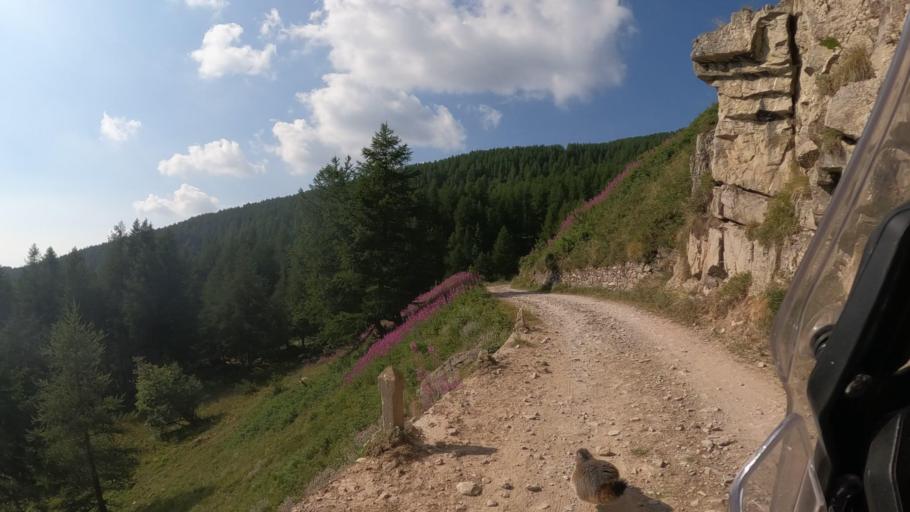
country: IT
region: Piedmont
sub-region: Provincia di Cuneo
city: Briga Alta
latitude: 44.1234
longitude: 7.6905
